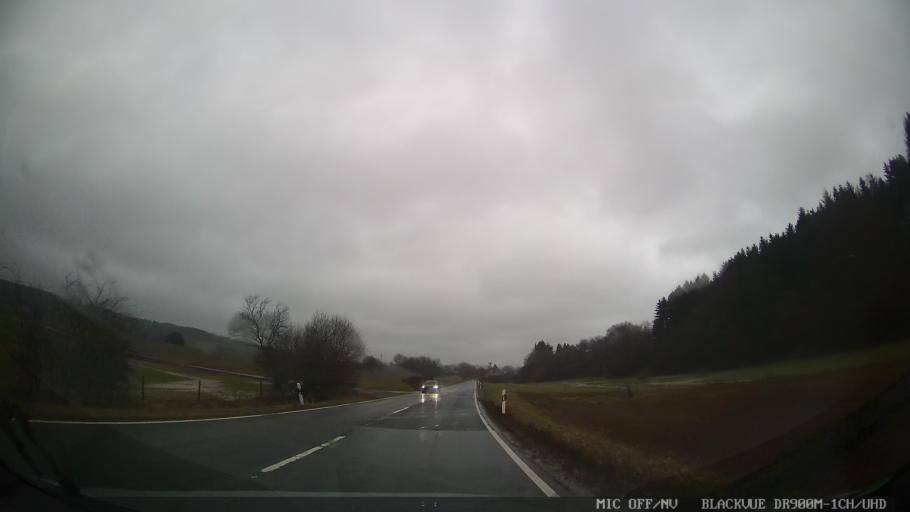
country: DE
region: Rheinland-Pfalz
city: Achtelsbach
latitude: 49.6205
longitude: 7.0814
